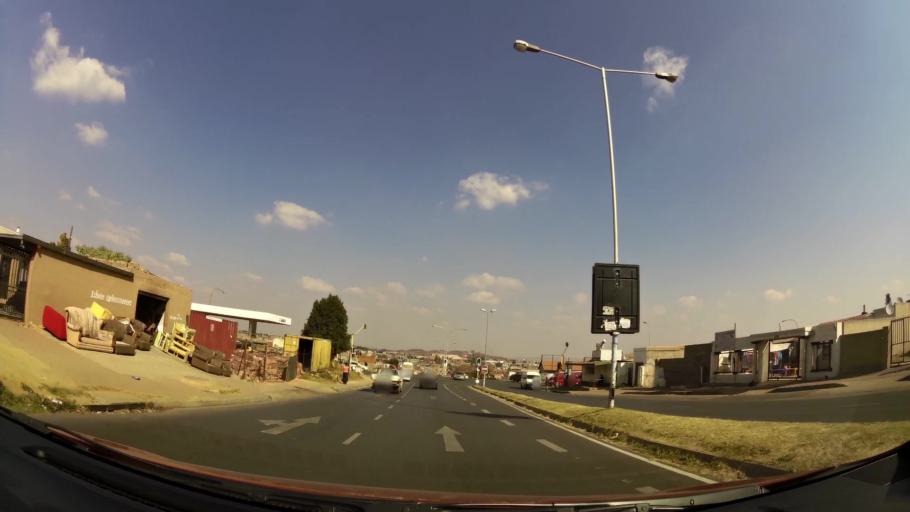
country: ZA
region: Gauteng
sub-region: City of Johannesburg Metropolitan Municipality
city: Soweto
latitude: -26.2476
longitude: 27.9483
